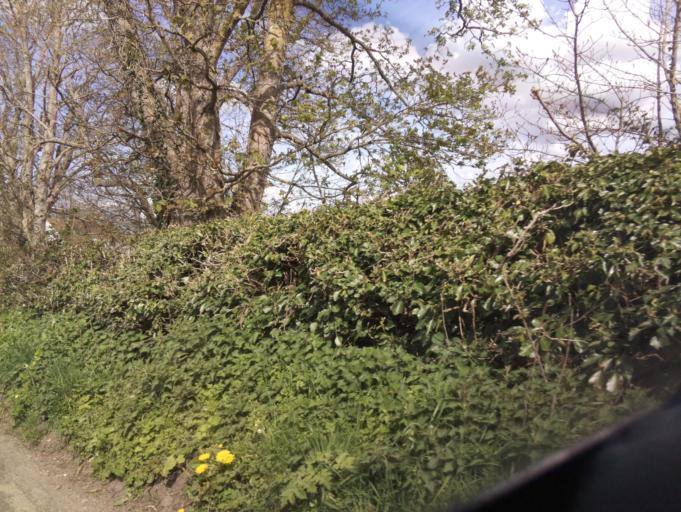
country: GB
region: England
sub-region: Hampshire
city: Abbotts Ann
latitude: 51.0974
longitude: -1.5118
